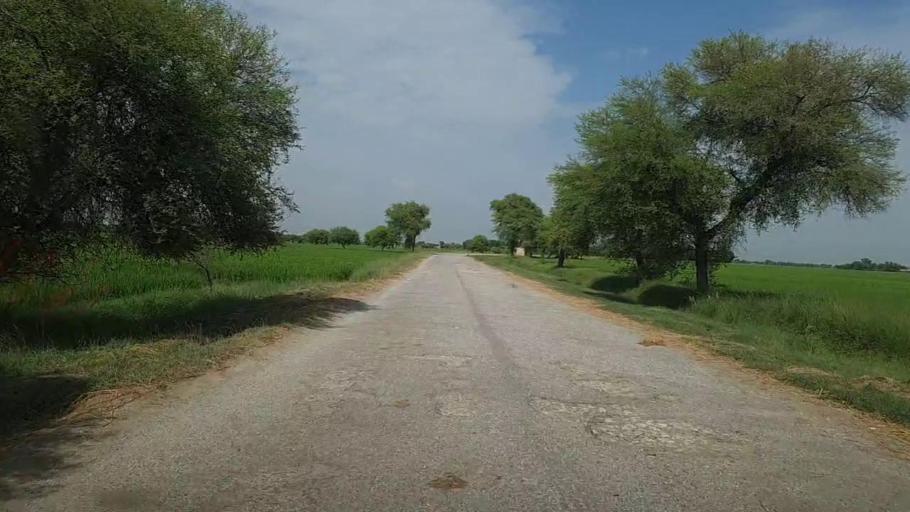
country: PK
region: Sindh
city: Thul
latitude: 28.2346
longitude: 68.7979
